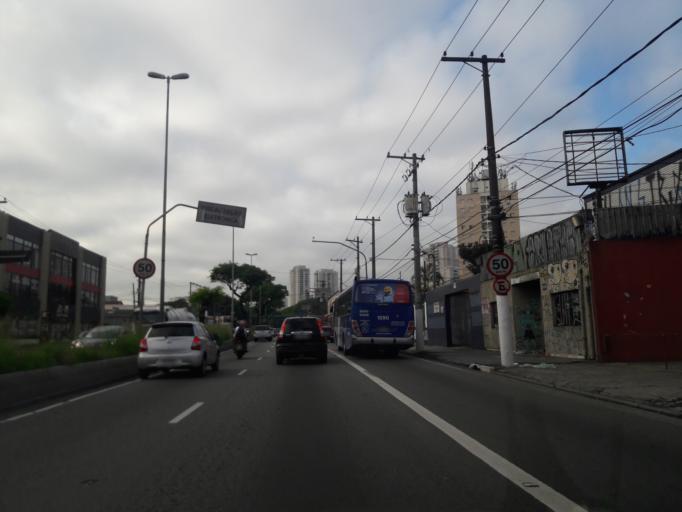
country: BR
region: Sao Paulo
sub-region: Sao Caetano Do Sul
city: Sao Caetano do Sul
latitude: -23.6173
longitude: -46.6018
